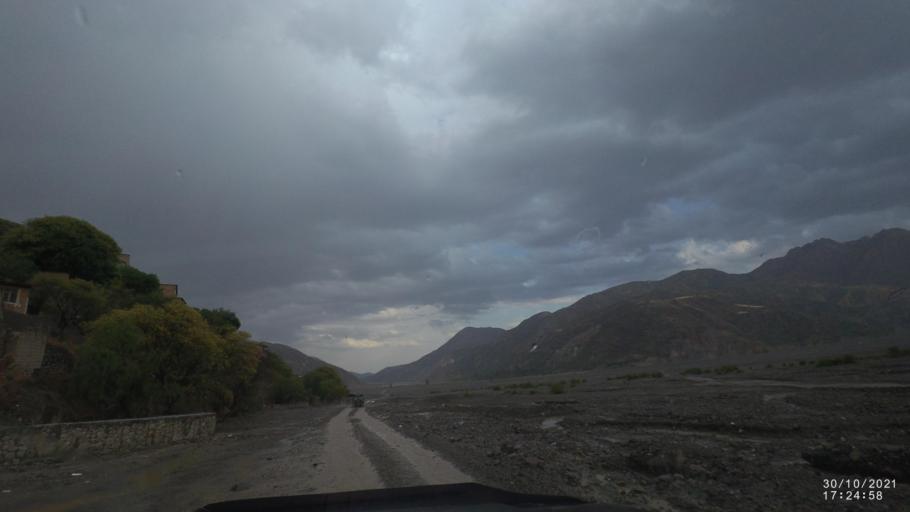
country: BO
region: Cochabamba
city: Colchani
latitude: -17.5173
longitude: -66.6220
